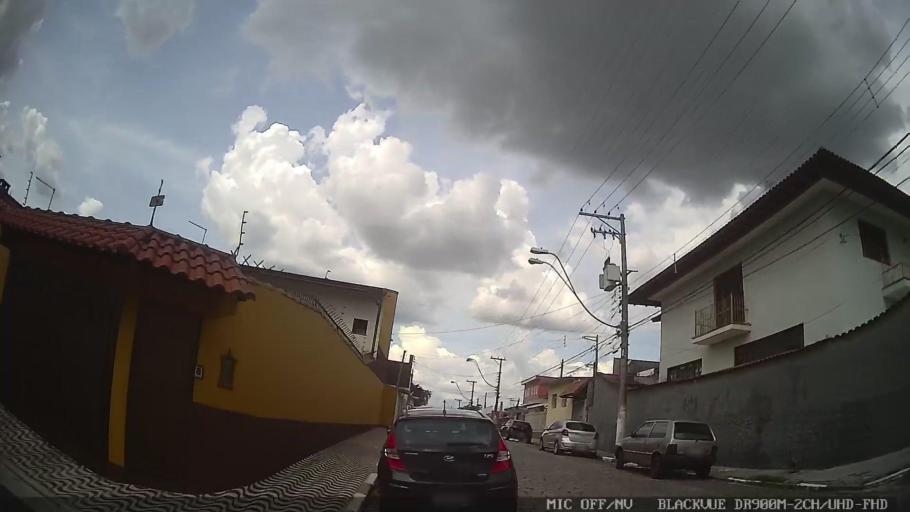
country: BR
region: Sao Paulo
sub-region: Poa
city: Poa
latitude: -23.5263
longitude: -46.3419
